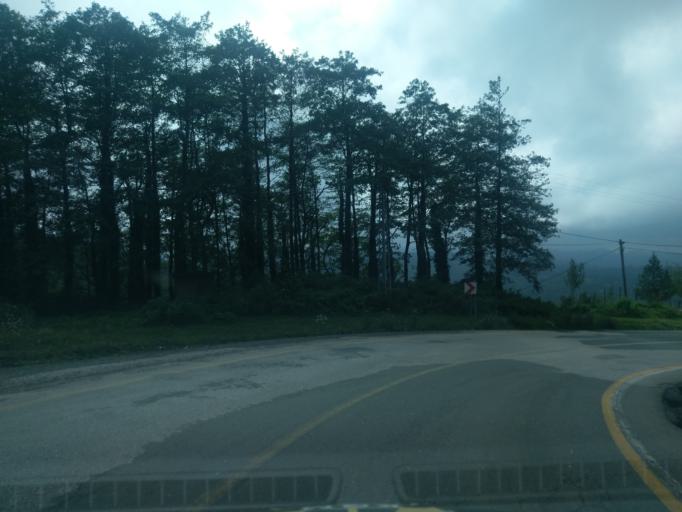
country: TR
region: Ordu
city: Gurgentepe
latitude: 40.8481
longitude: 37.6550
